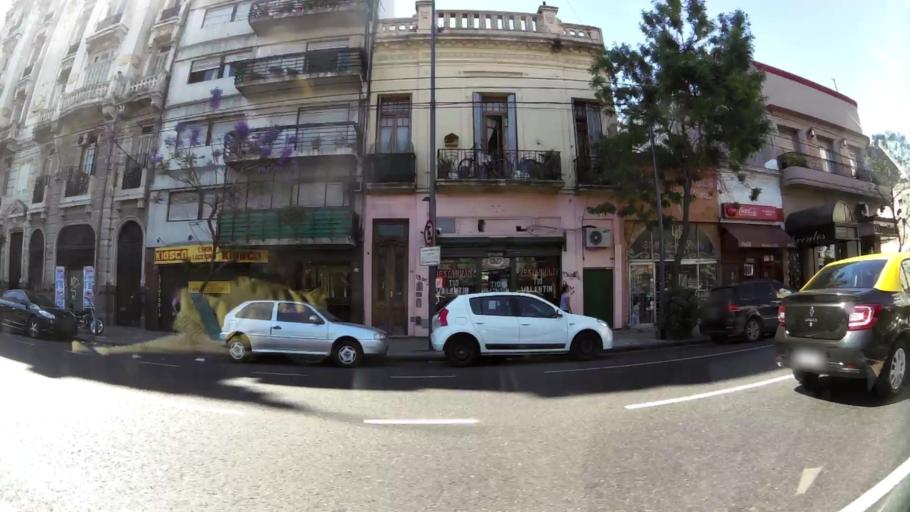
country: AR
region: Buenos Aires F.D.
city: Buenos Aires
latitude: -34.6232
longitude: -58.3981
